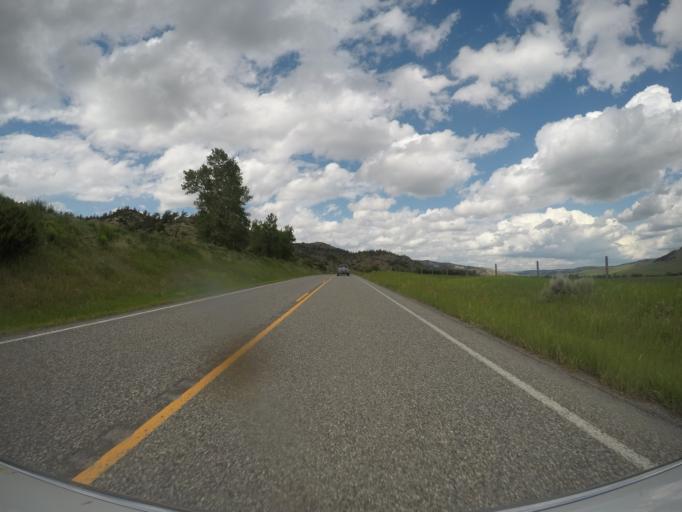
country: US
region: Montana
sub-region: Sweet Grass County
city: Big Timber
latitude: 45.6806
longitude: -110.0863
